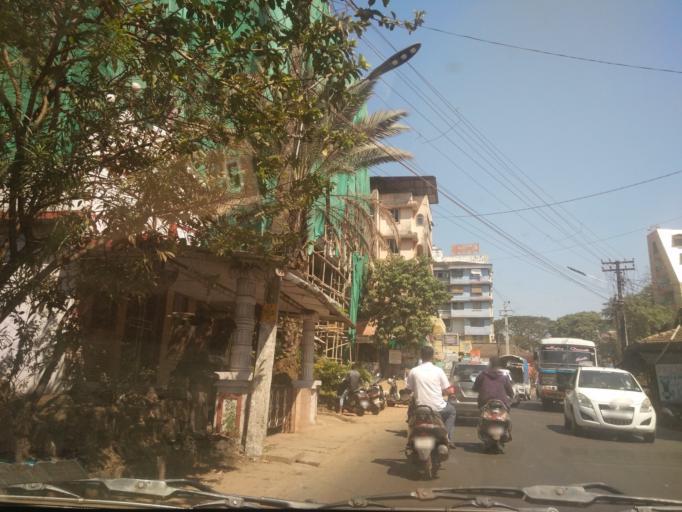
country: IN
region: Goa
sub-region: North Goa
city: Mapuca
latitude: 15.5923
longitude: 73.8131
